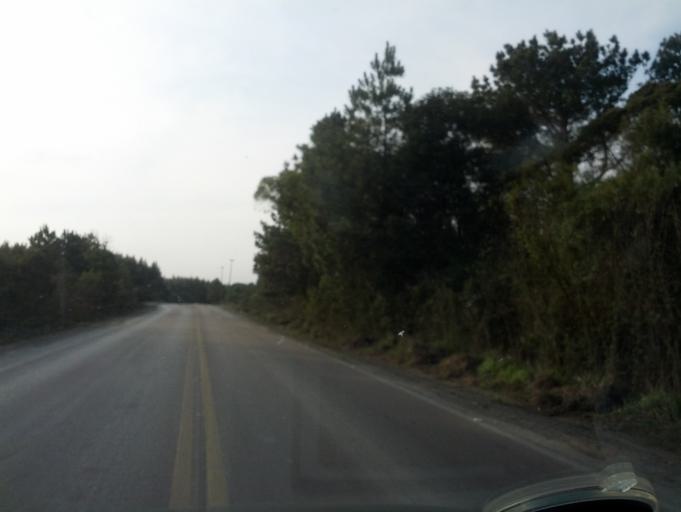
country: BR
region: Santa Catarina
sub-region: Otacilio Costa
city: Otacilio Costa
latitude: -27.4474
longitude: -50.1247
